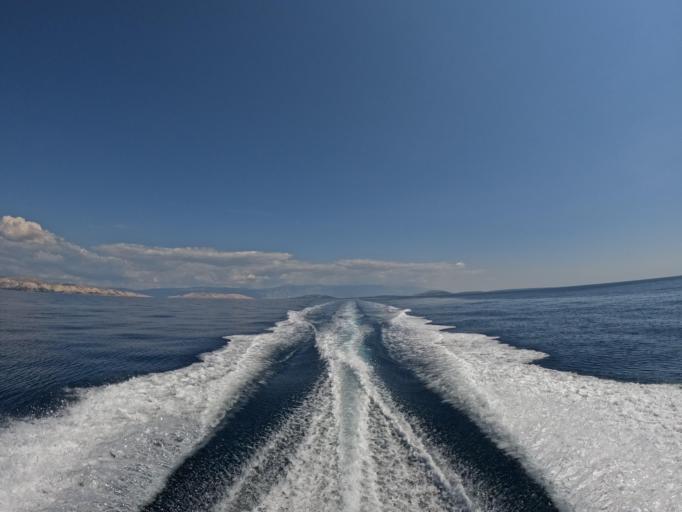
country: HR
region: Primorsko-Goranska
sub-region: Grad Krk
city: Krk
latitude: 44.9178
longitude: 14.5732
